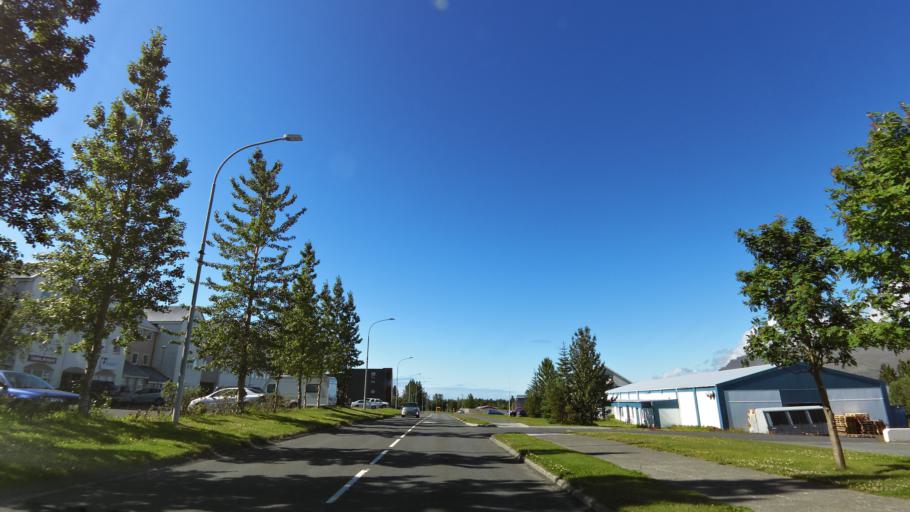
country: IS
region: Capital Region
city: Mosfellsbaer
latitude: 64.1676
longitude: -21.6989
